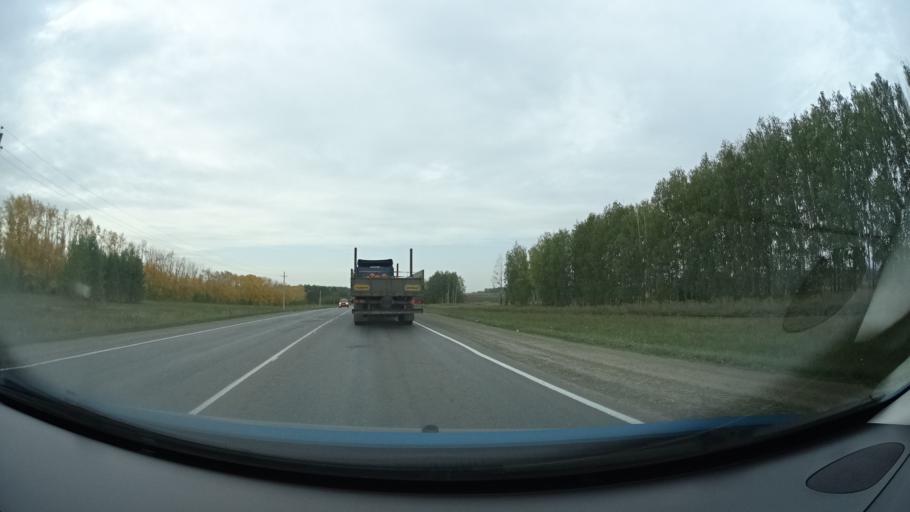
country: RU
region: Bashkortostan
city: Buzdyak
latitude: 54.6913
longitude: 54.8189
